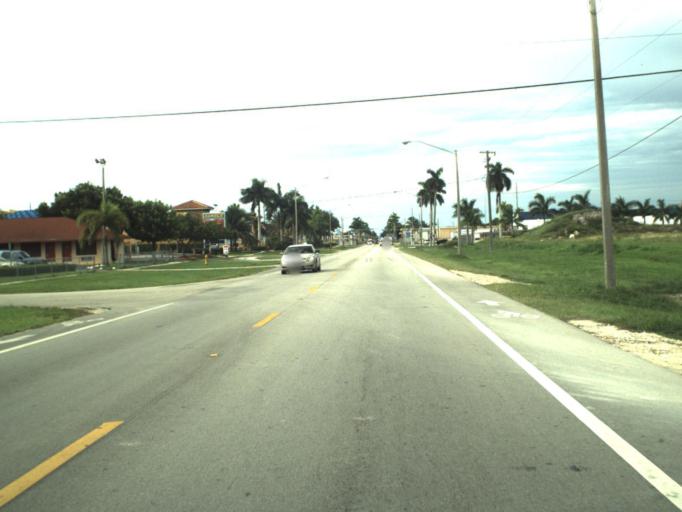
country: US
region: Florida
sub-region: Miami-Dade County
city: Homestead
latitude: 25.4589
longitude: -80.4772
